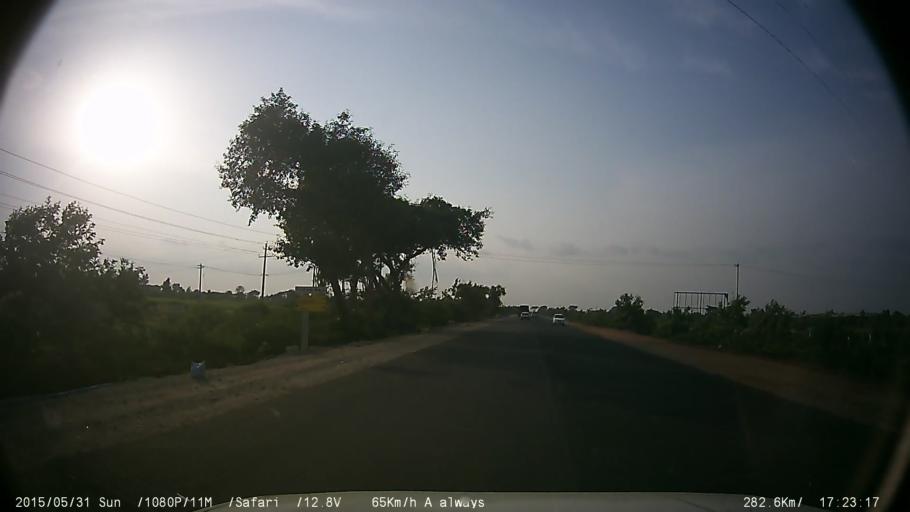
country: IN
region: Karnataka
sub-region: Chamrajnagar
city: Gundlupet
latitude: 11.8384
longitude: 76.6750
